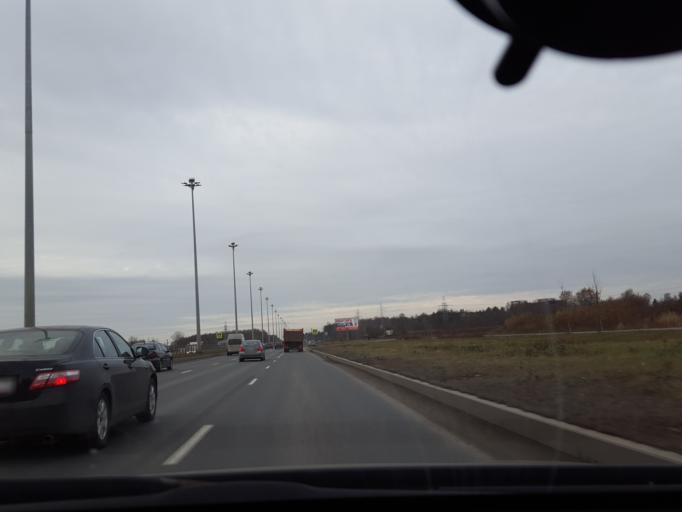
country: RU
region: Leningrad
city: Untolovo
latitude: 60.0401
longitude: 30.2419
